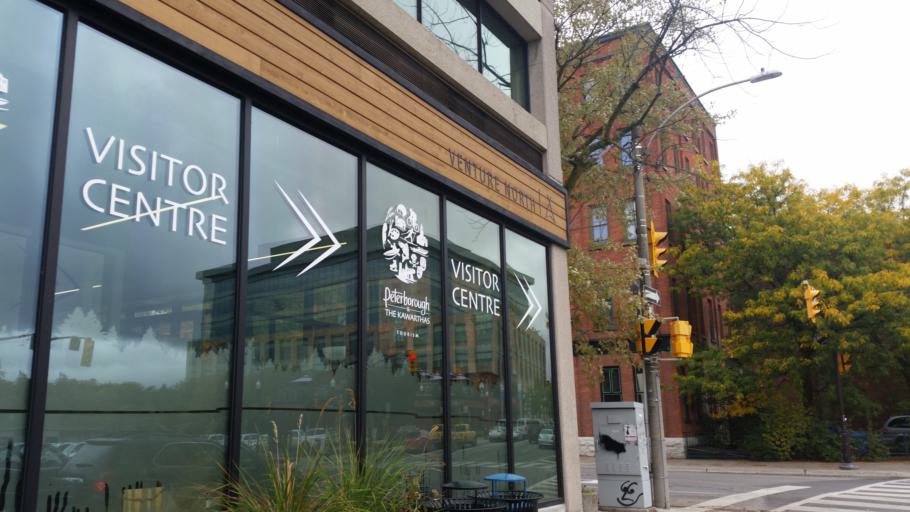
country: CA
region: Ontario
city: Peterborough
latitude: 44.3019
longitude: -78.3191
